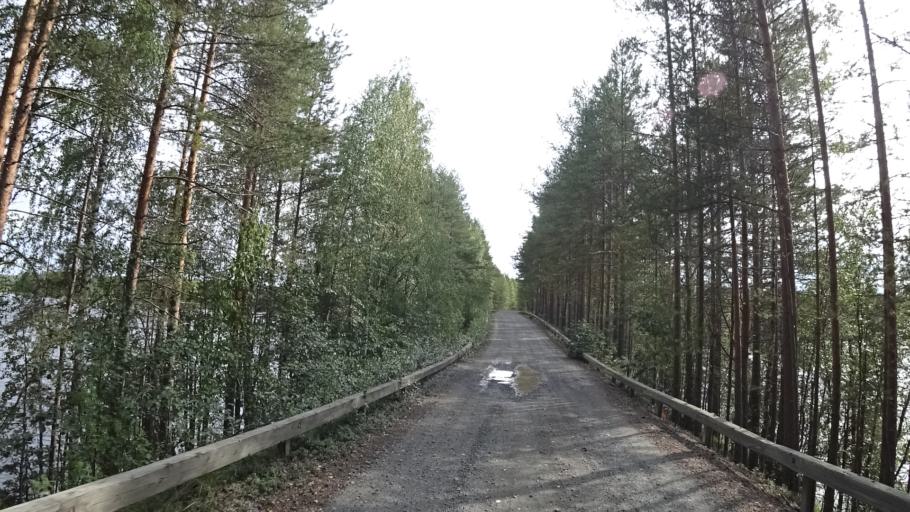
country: FI
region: North Karelia
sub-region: Joensuu
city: Ilomantsi
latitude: 62.6167
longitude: 31.1962
